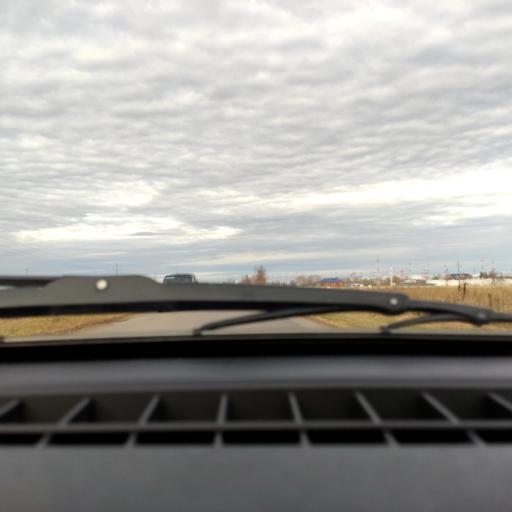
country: RU
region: Bashkortostan
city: Blagoveshchensk
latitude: 54.8946
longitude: 56.1511
